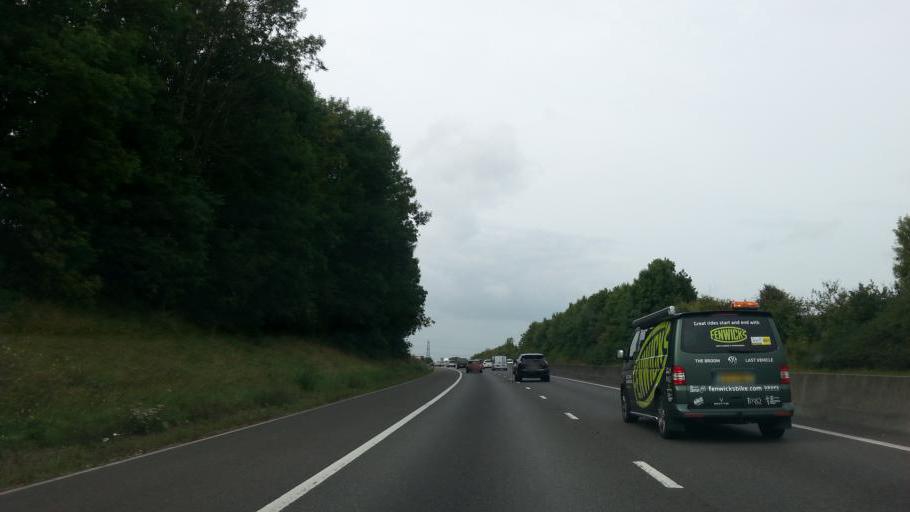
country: GB
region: England
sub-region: Essex
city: Elsenham
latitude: 51.9345
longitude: 0.2239
